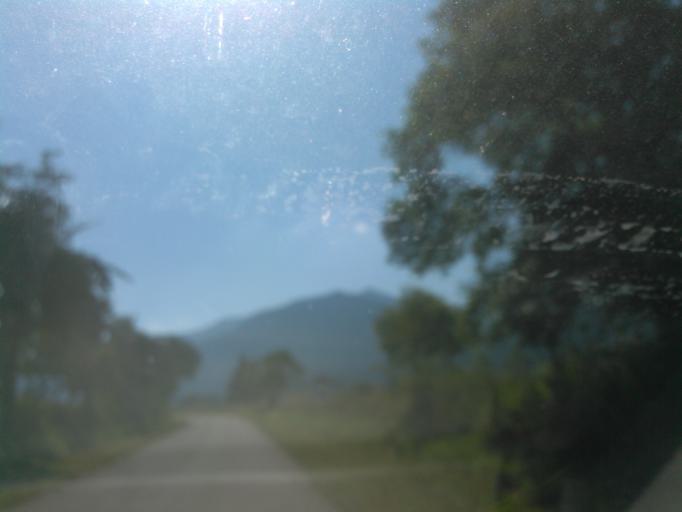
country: SK
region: Zilinsky
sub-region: Okres Liptovsky Mikulas
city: Liptovsky Mikulas
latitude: 49.0267
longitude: 19.5093
